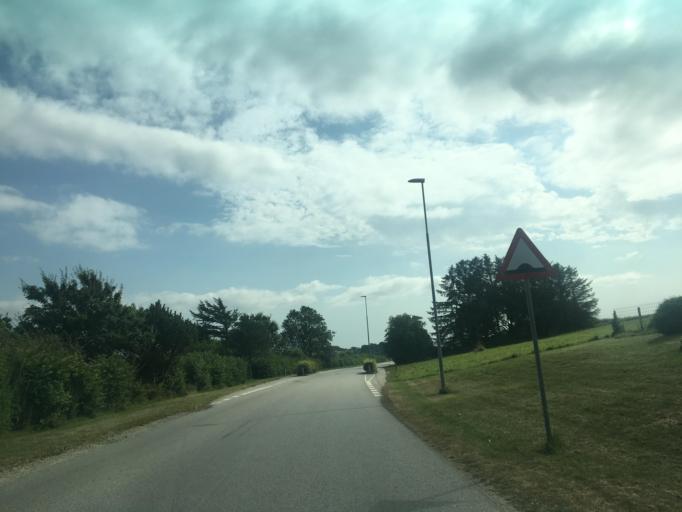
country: DK
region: North Denmark
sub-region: Thisted Kommune
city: Thisted
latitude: 56.8761
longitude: 8.6282
